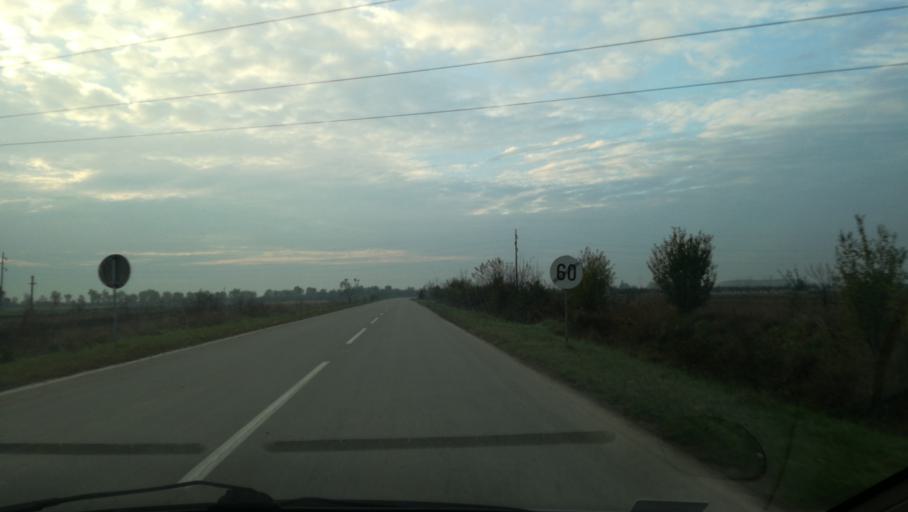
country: RS
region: Autonomna Pokrajina Vojvodina
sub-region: Severnobanatski Okrug
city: Kikinda
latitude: 45.8042
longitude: 20.4361
